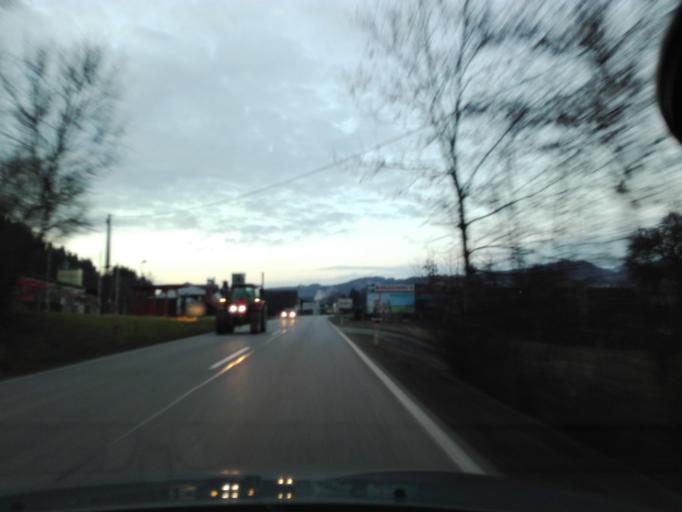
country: AT
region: Upper Austria
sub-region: Politischer Bezirk Perg
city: Bad Kreuzen
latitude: 48.2171
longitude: 14.8550
